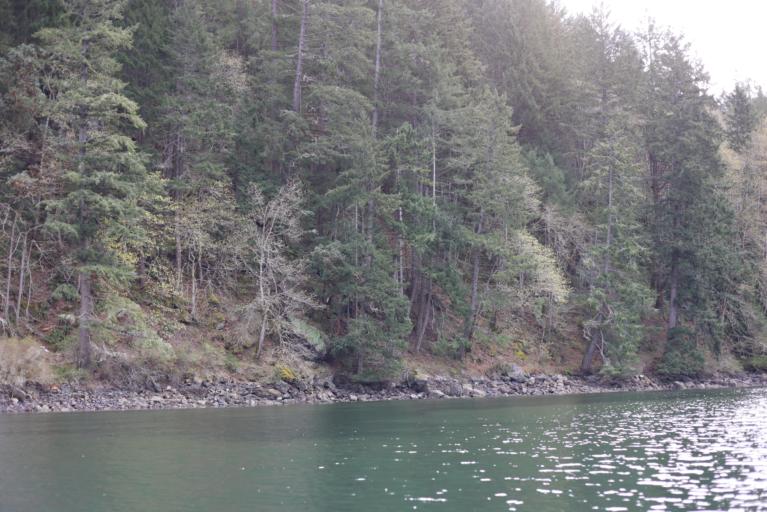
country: CA
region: British Columbia
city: Langford
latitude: 48.4974
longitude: -123.5485
